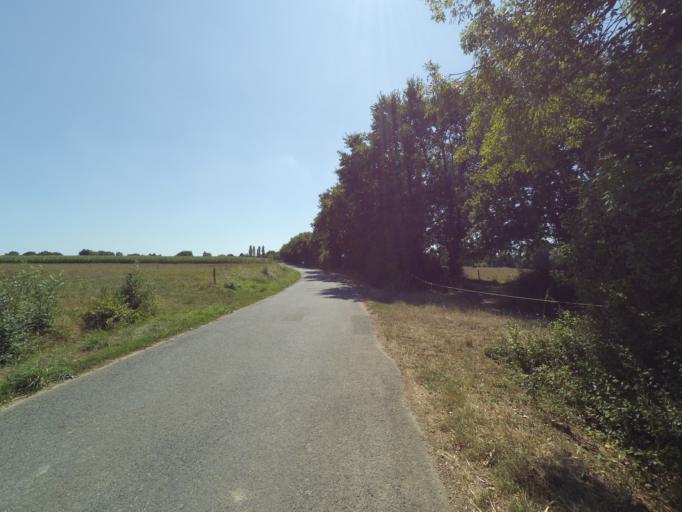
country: FR
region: Pays de la Loire
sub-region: Departement de la Loire-Atlantique
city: Vieillevigne
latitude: 46.9844
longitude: -1.4239
